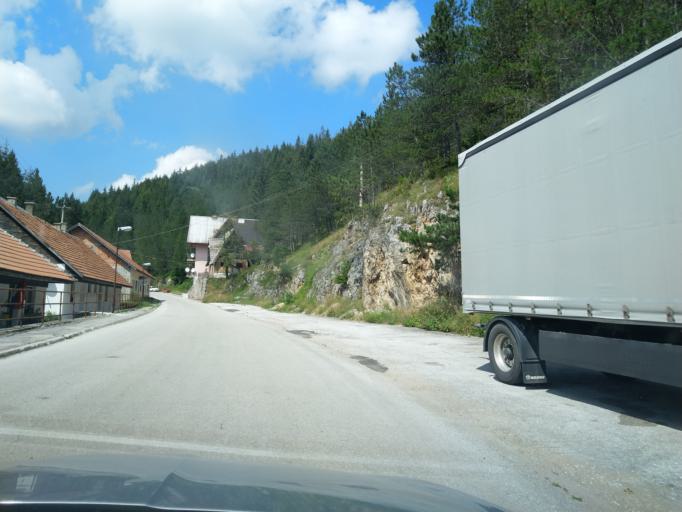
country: RS
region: Central Serbia
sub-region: Zlatiborski Okrug
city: Nova Varos
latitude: 43.5471
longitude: 19.9029
